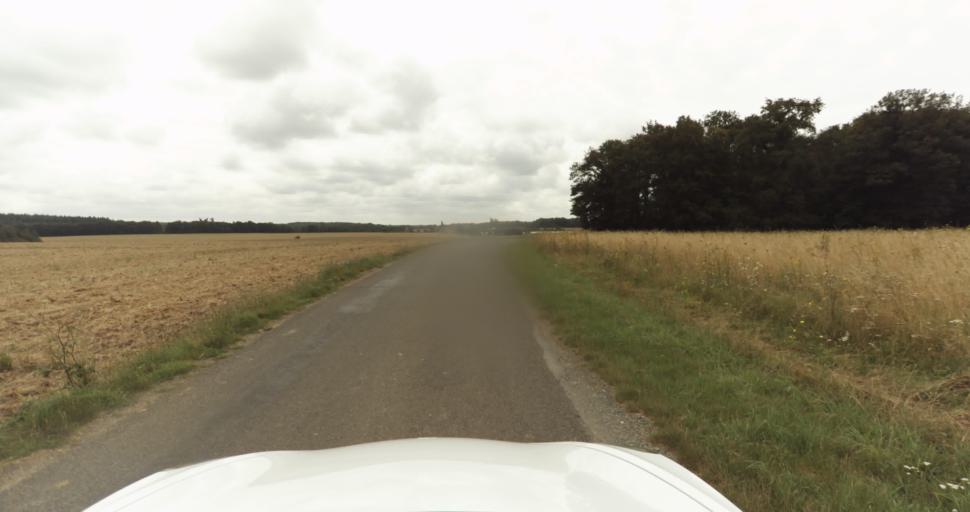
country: FR
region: Haute-Normandie
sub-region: Departement de l'Eure
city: Saint-Sebastien-de-Morsent
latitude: 49.0248
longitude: 1.0620
